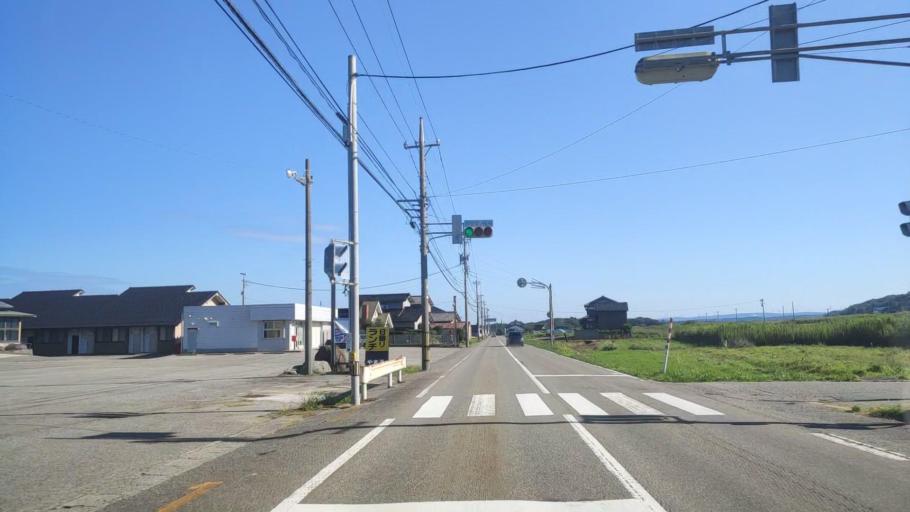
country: JP
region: Ishikawa
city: Hakui
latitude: 36.9389
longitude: 136.7600
